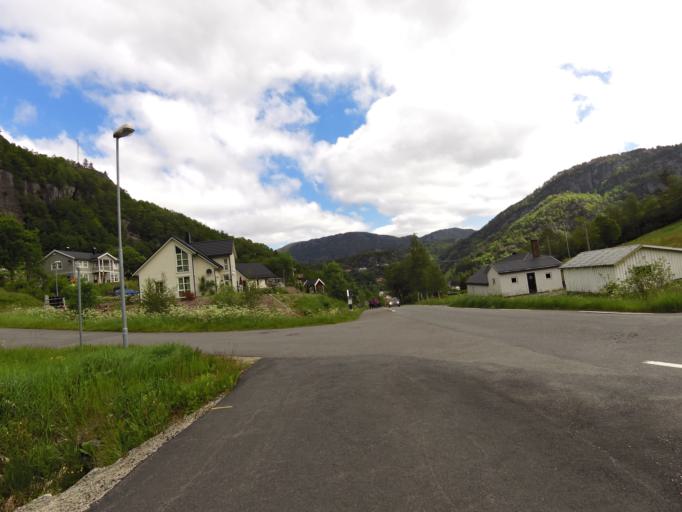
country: NO
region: Vest-Agder
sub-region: Flekkefjord
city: Flekkefjord
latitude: 58.2680
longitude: 6.8078
